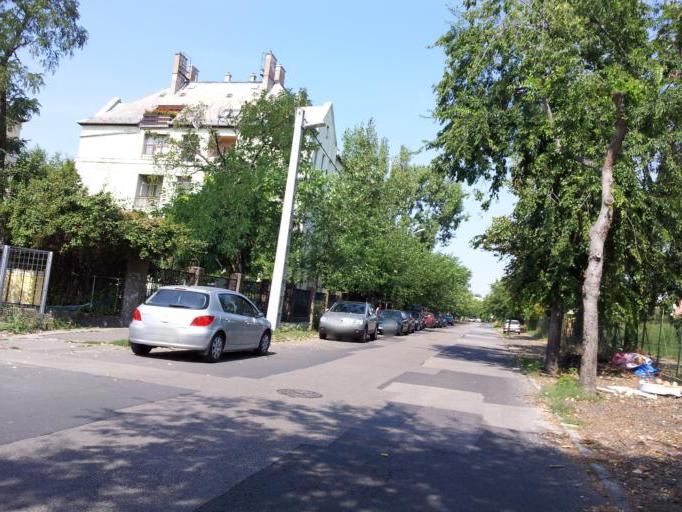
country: HU
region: Budapest
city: Budapest XIV. keruelet
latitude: 47.5086
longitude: 19.1155
